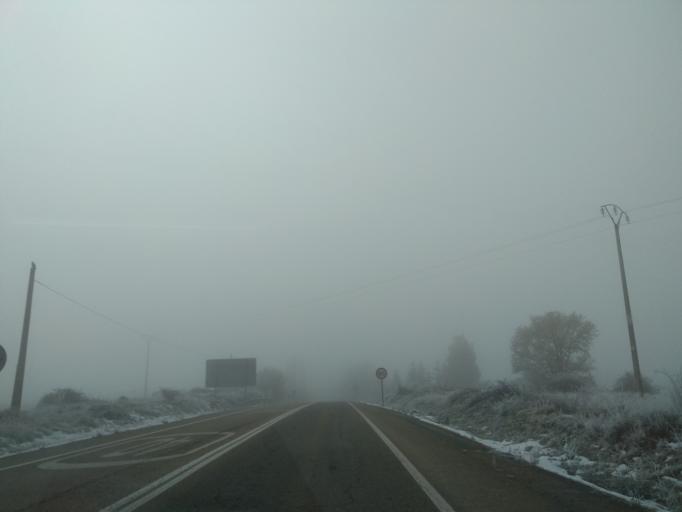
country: ES
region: Castille and Leon
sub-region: Provincia de Burgos
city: Espinosa de los Monteros
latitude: 43.0478
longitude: -3.4868
